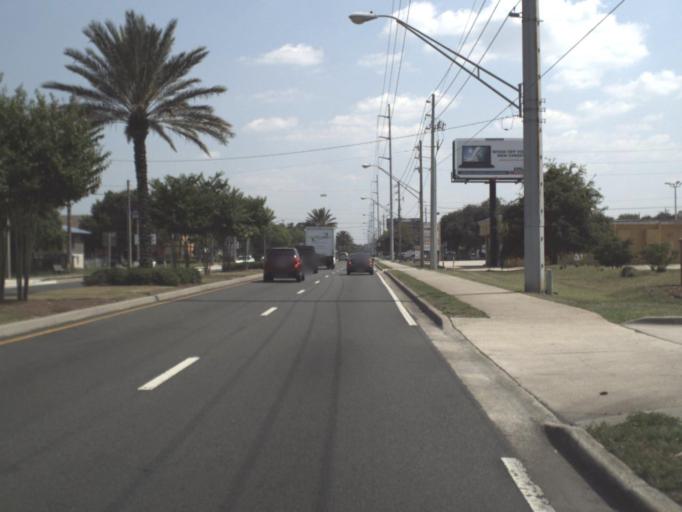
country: US
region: Florida
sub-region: Duval County
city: Atlantic Beach
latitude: 30.3525
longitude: -81.4138
